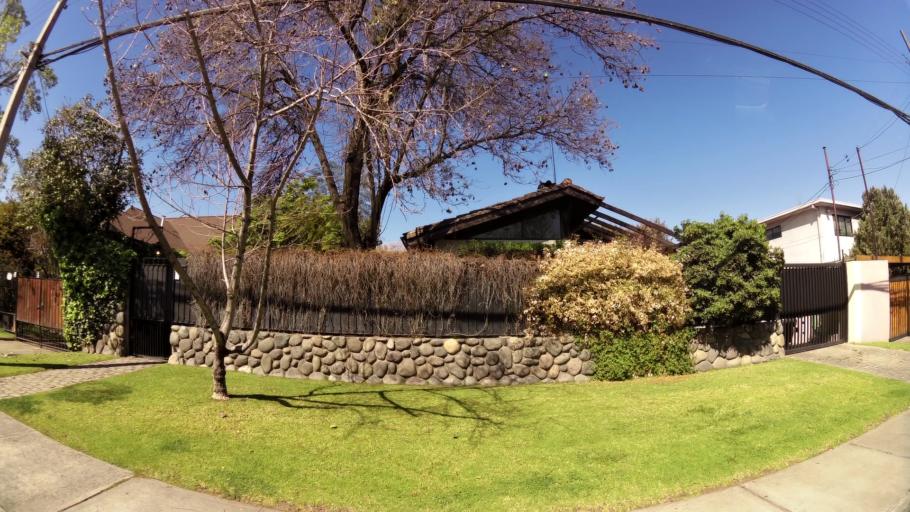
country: CL
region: Santiago Metropolitan
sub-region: Provincia de Santiago
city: Villa Presidente Frei, Nunoa, Santiago, Chile
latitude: -33.3957
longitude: -70.5529
